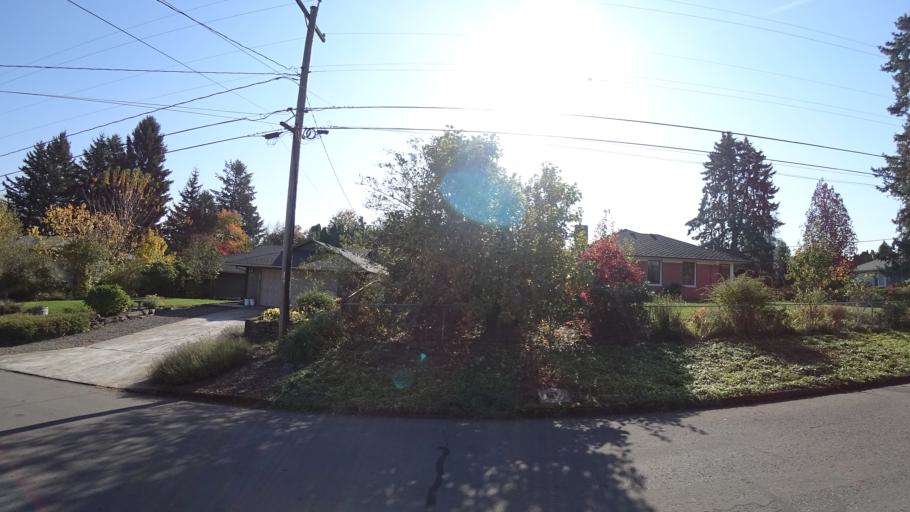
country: US
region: Oregon
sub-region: Multnomah County
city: Gresham
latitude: 45.5029
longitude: -122.4420
